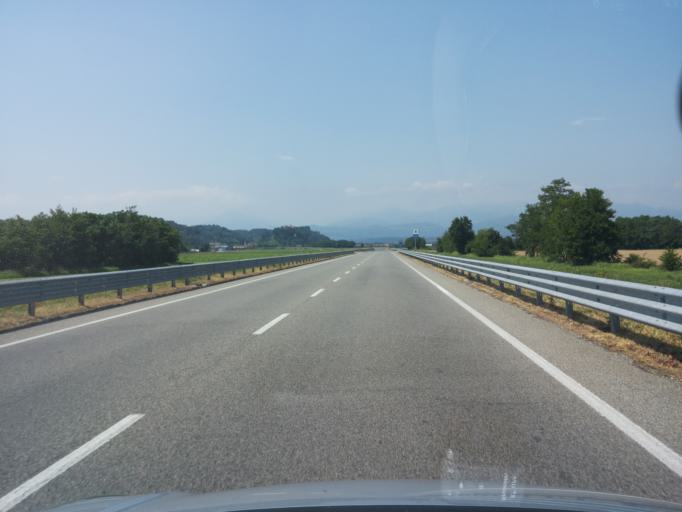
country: IT
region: Piedmont
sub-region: Provincia di Biella
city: Castelletto Cervo
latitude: 45.5198
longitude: 8.2059
